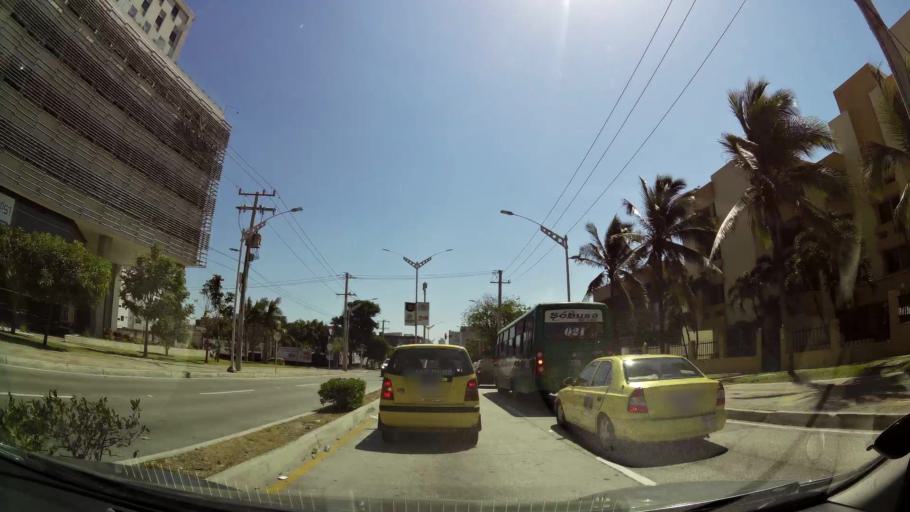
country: CO
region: Atlantico
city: Barranquilla
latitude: 11.0095
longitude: -74.8253
